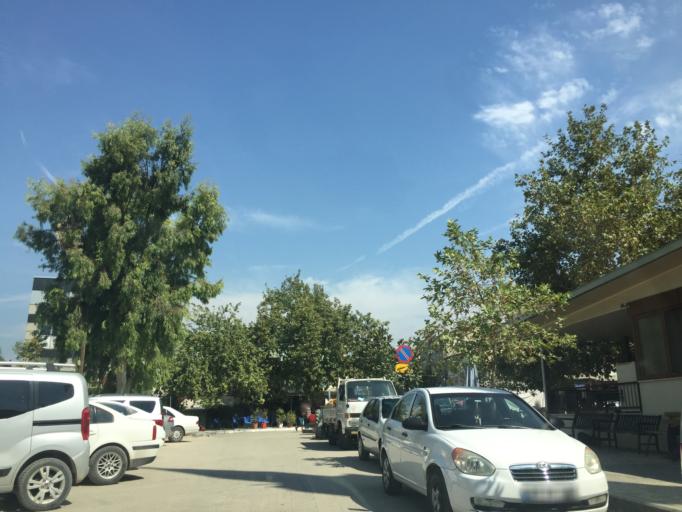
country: TR
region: Izmir
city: Bornova
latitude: 38.4275
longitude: 27.2658
